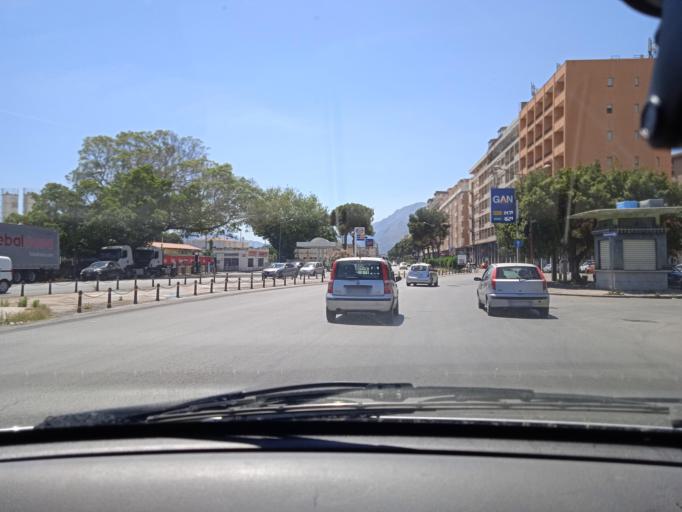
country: IT
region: Sicily
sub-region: Palermo
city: Palermo
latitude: 38.1311
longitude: 13.3602
